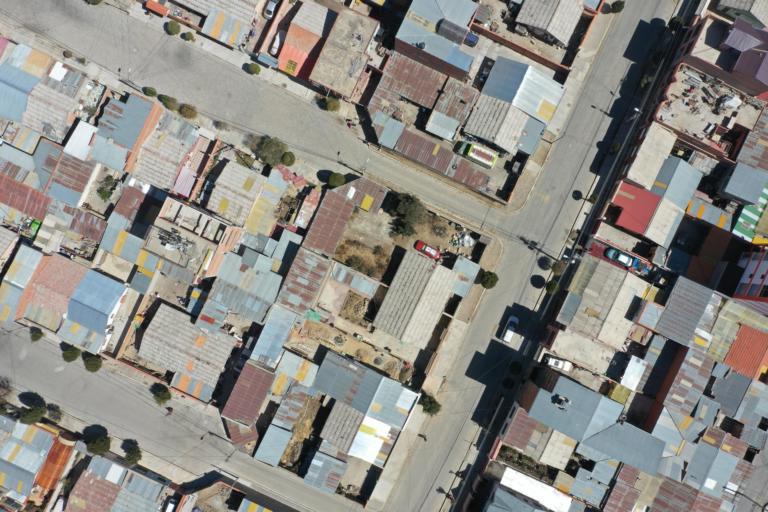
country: BO
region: La Paz
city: La Paz
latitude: -16.5329
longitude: -68.1523
